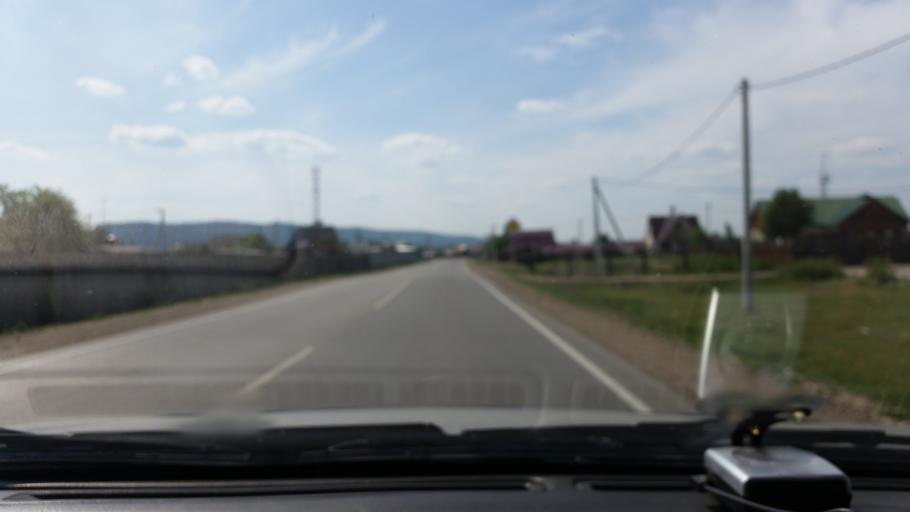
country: RU
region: Irkutsk
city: Baklashi
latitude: 52.2049
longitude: 103.9491
